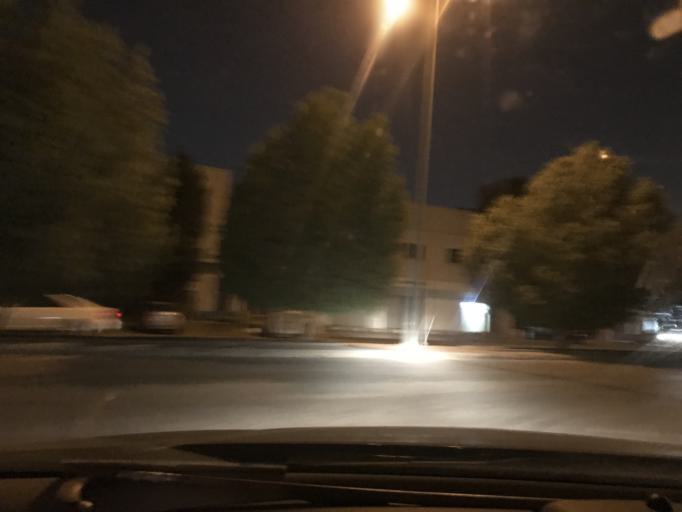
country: SA
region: Ar Riyad
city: Riyadh
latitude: 24.7485
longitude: 46.7588
